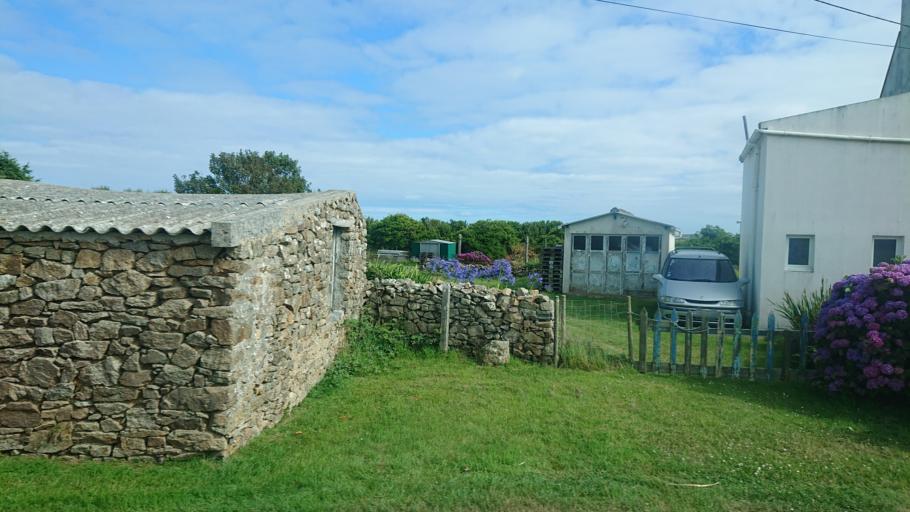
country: FR
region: Brittany
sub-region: Departement du Finistere
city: Porspoder
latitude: 48.4674
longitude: -5.0737
